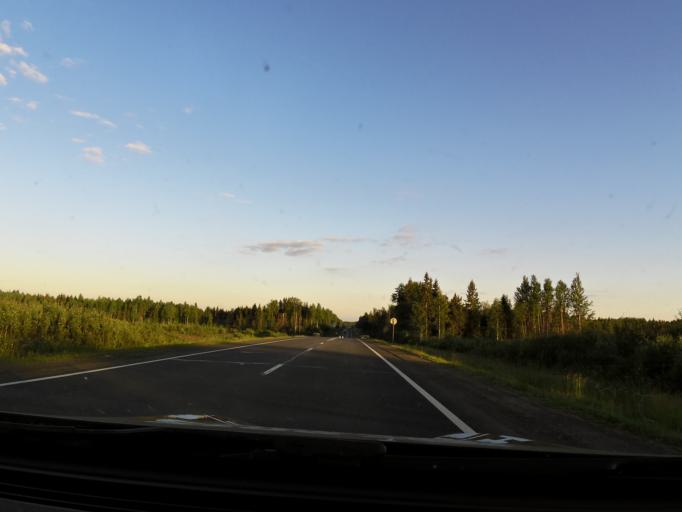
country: RU
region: Jaroslavl
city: Prechistoye
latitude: 58.5707
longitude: 40.3542
